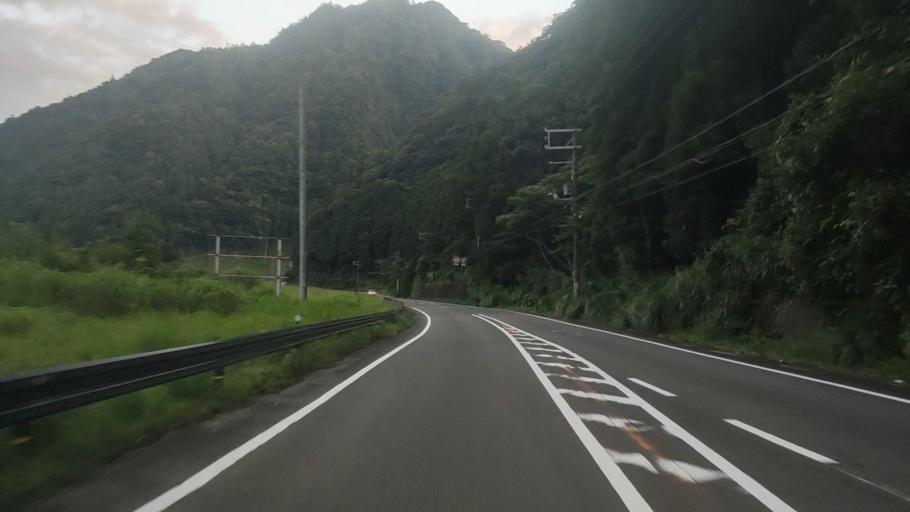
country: JP
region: Wakayama
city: Shingu
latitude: 33.7887
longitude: 135.8959
